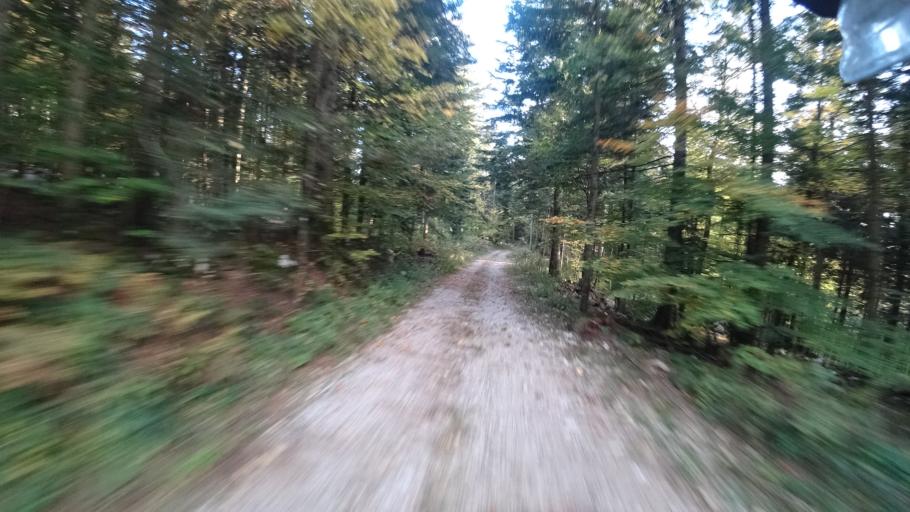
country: HR
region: Karlovacka
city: Plaski
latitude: 45.0204
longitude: 15.4337
